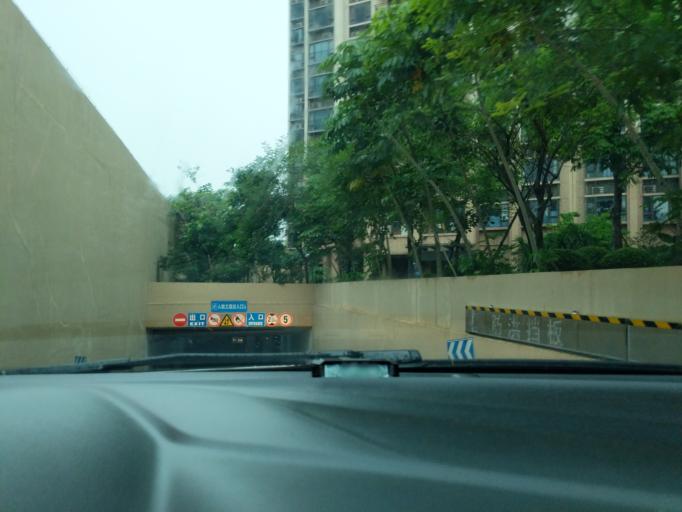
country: CN
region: Guangdong
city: Huangge
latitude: 22.7997
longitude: 113.5142
